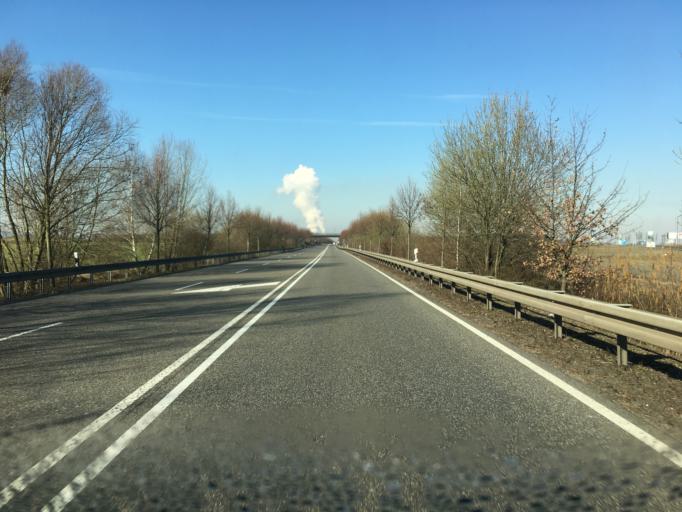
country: DE
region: North Rhine-Westphalia
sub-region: Regierungsbezirk Koln
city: Pulheim
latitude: 50.9841
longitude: 6.8187
